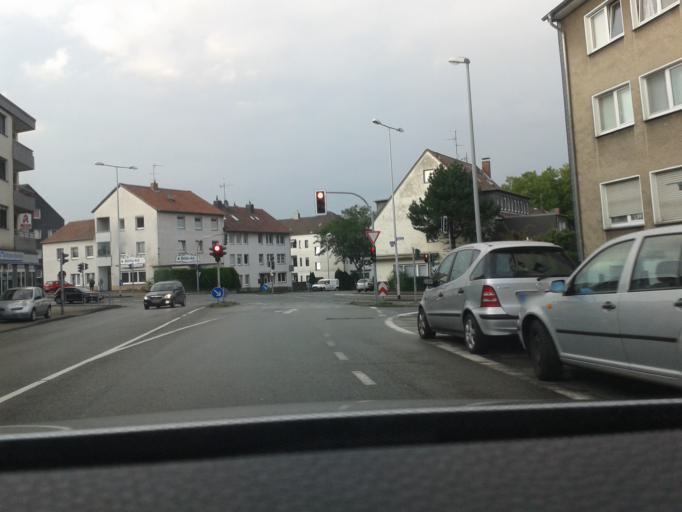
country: DE
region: North Rhine-Westphalia
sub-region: Regierungsbezirk Dusseldorf
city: Muelheim (Ruhr)
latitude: 51.4271
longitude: 6.8293
